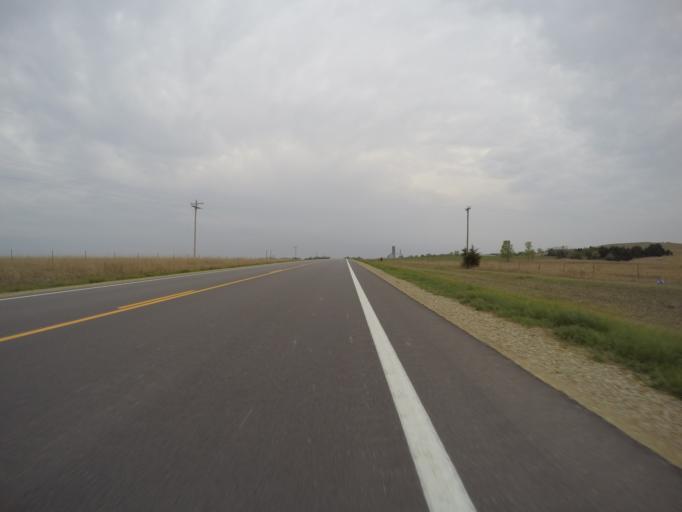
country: US
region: Kansas
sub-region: Pottawatomie County
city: Westmoreland
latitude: 39.3545
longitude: -96.5198
